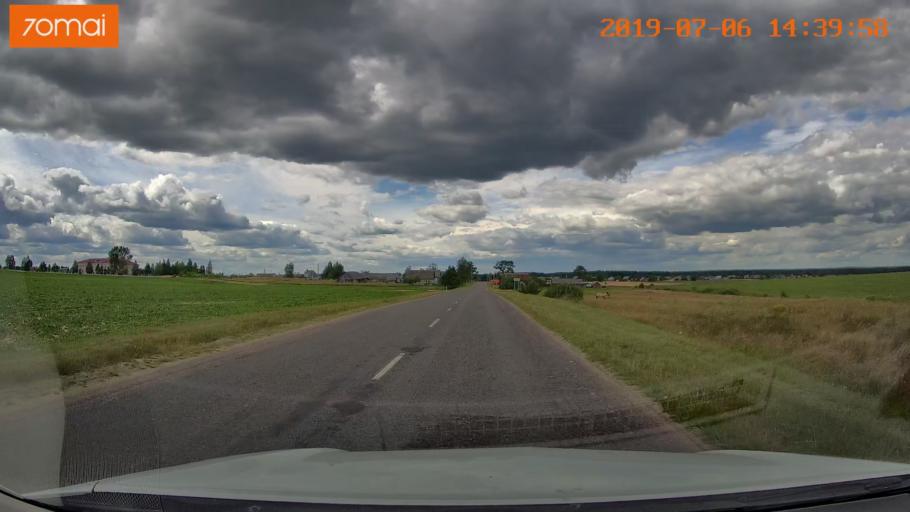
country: BY
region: Minsk
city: Ivyanyets
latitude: 53.9212
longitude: 26.6797
